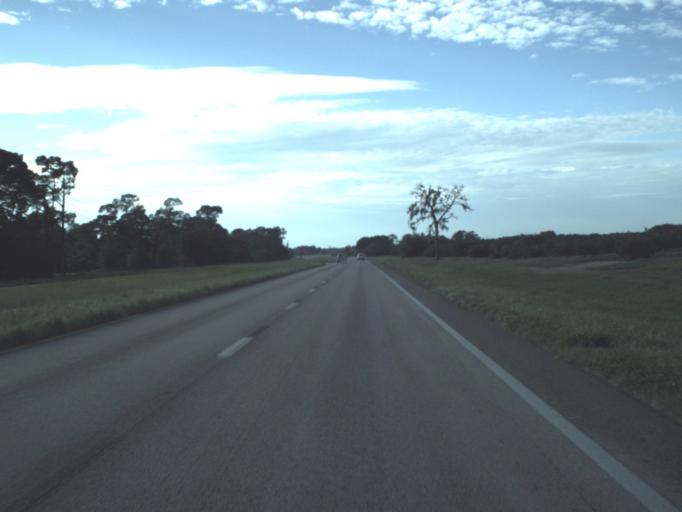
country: US
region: Florida
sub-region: Highlands County
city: Lake Placid
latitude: 27.2464
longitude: -81.3373
